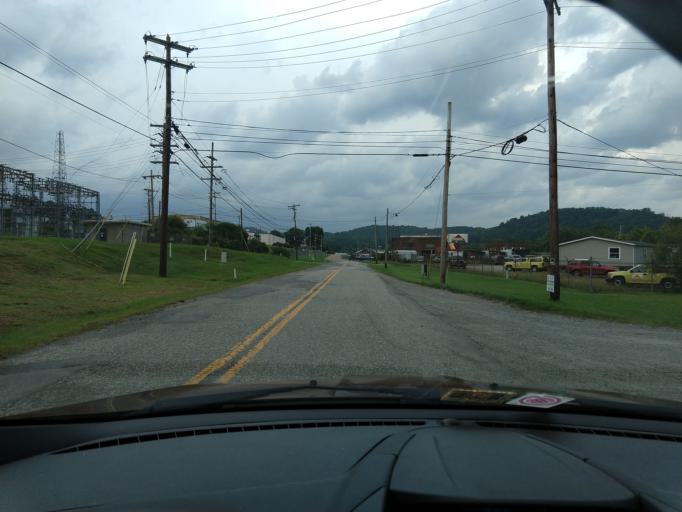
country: US
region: West Virginia
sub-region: Harrison County
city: Clarksburg
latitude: 39.2651
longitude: -80.3637
